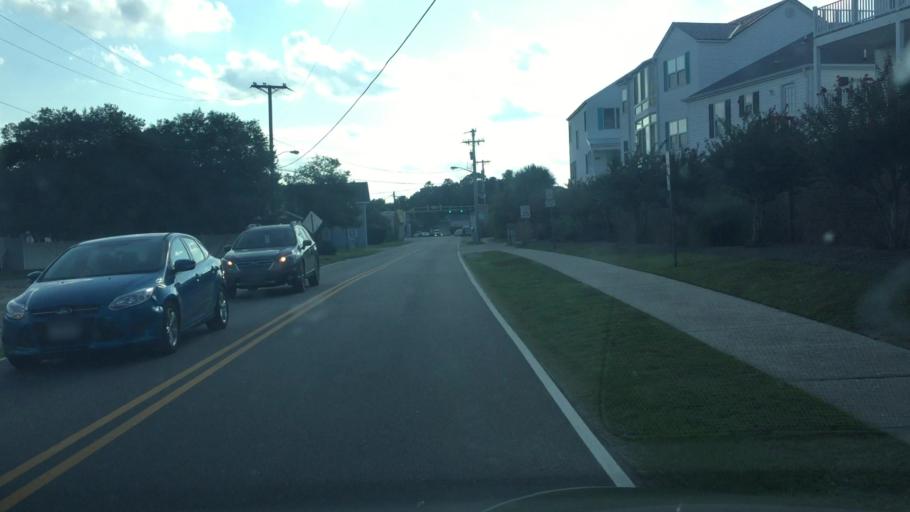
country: US
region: South Carolina
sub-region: Horry County
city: North Myrtle Beach
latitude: 33.8212
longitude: -78.6712
